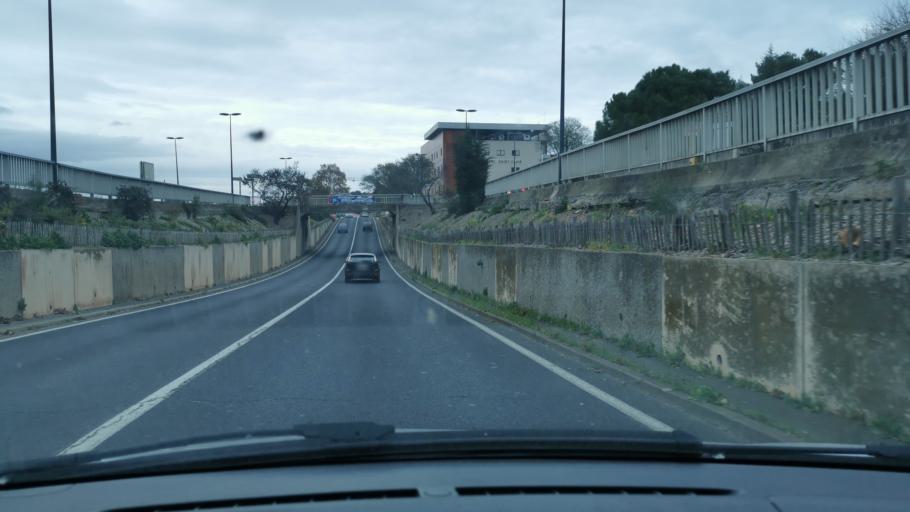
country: FR
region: Languedoc-Roussillon
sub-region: Departement de l'Herault
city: Sete
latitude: 43.4074
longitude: 3.6676
